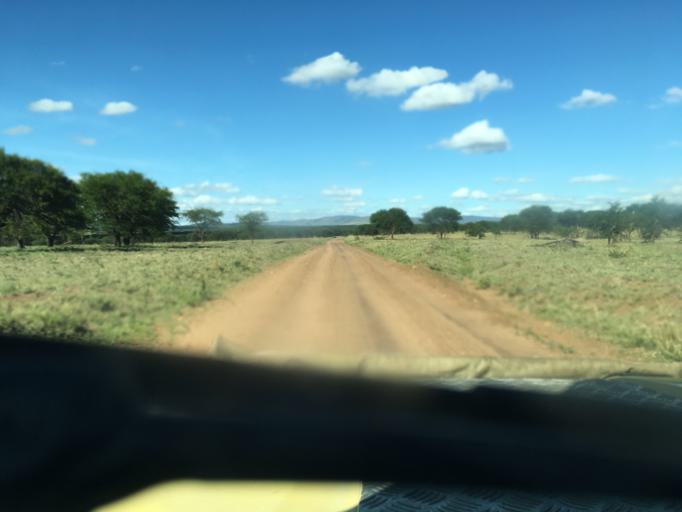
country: TZ
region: Mara
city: Mugumu
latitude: -2.0739
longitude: 35.1164
